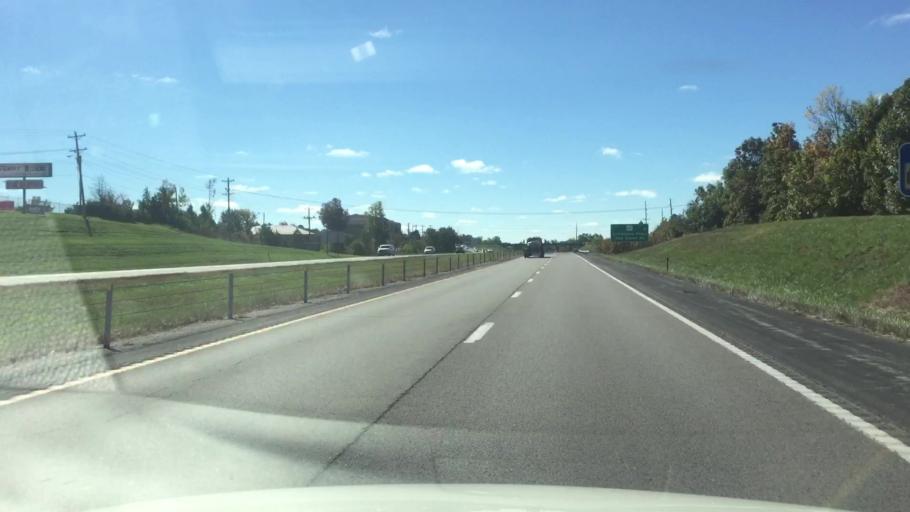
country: US
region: Missouri
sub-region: Boone County
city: Columbia
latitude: 38.9193
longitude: -92.2942
